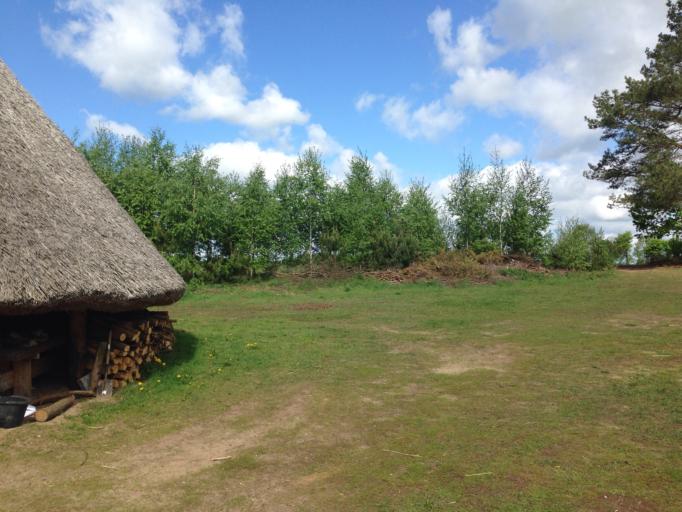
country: PL
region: Podlasie
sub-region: Powiat lomzynski
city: Wizna
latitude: 53.2861
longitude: 22.4590
